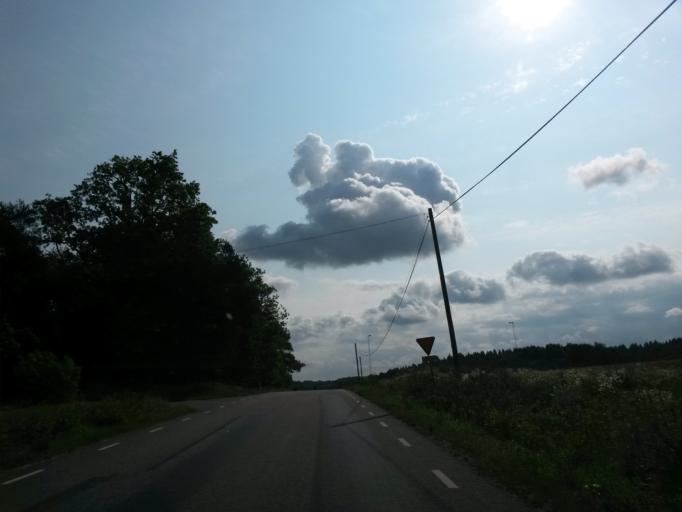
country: SE
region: Vaestra Goetaland
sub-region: Vargarda Kommun
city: Jonstorp
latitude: 58.0038
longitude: 12.7268
